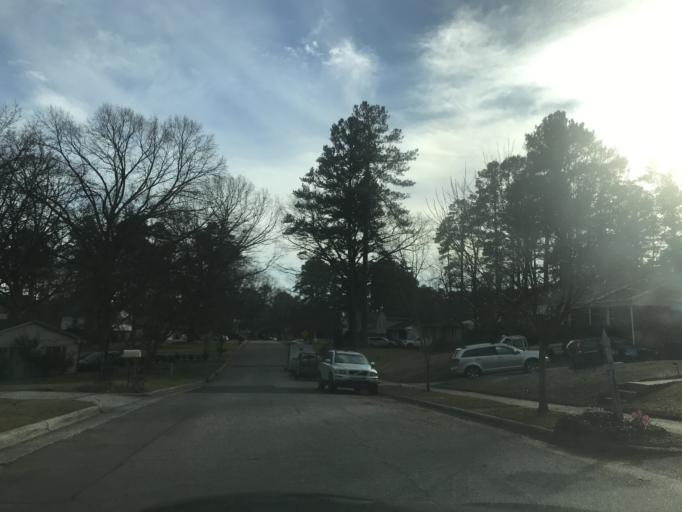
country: US
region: North Carolina
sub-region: Wake County
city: Raleigh
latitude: 35.8297
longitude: -78.5928
